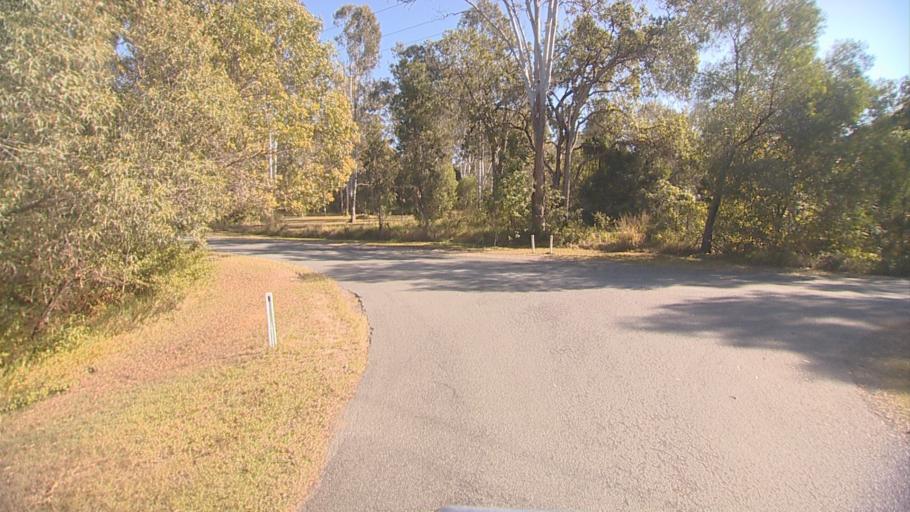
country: AU
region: Queensland
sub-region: Logan
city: Cedar Vale
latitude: -27.8309
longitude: 153.0429
